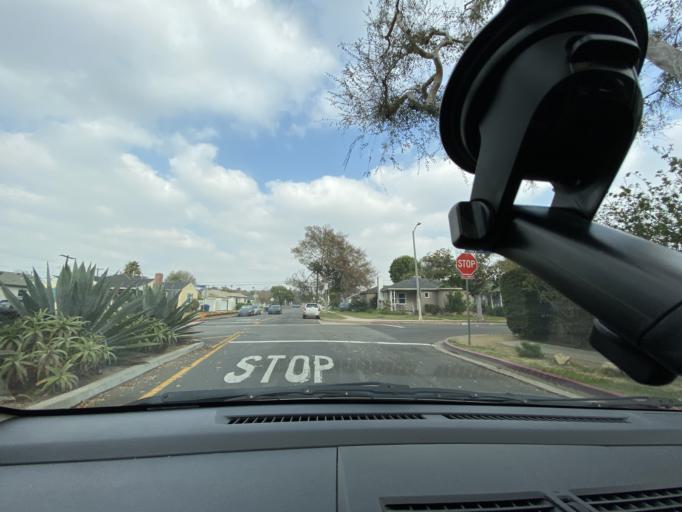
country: US
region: California
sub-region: Los Angeles County
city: Culver City
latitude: 34.0346
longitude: -118.3946
